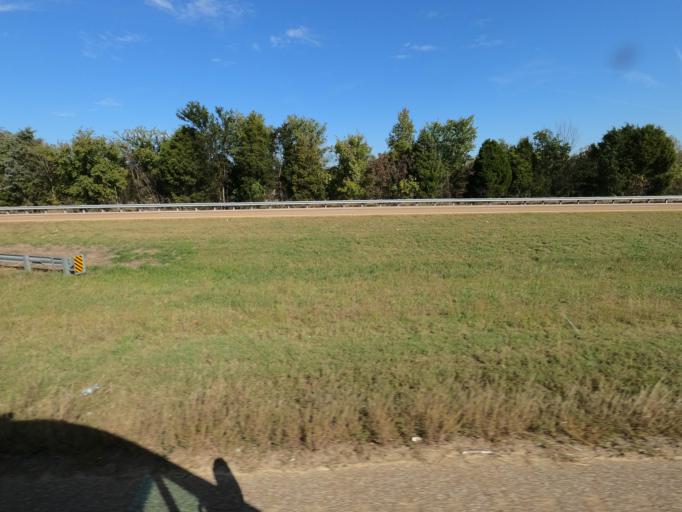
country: US
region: Tennessee
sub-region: Shelby County
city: Millington
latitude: 35.3301
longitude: -89.8978
